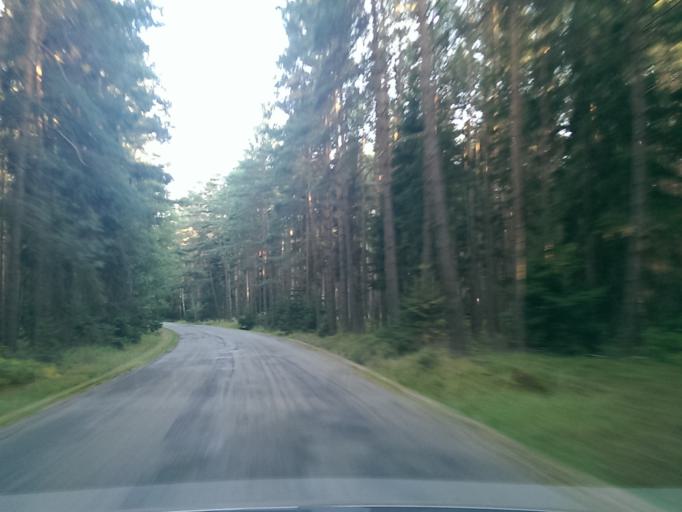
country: CZ
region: Central Bohemia
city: Bela pod Bezdezem
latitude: 50.5031
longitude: 14.7200
